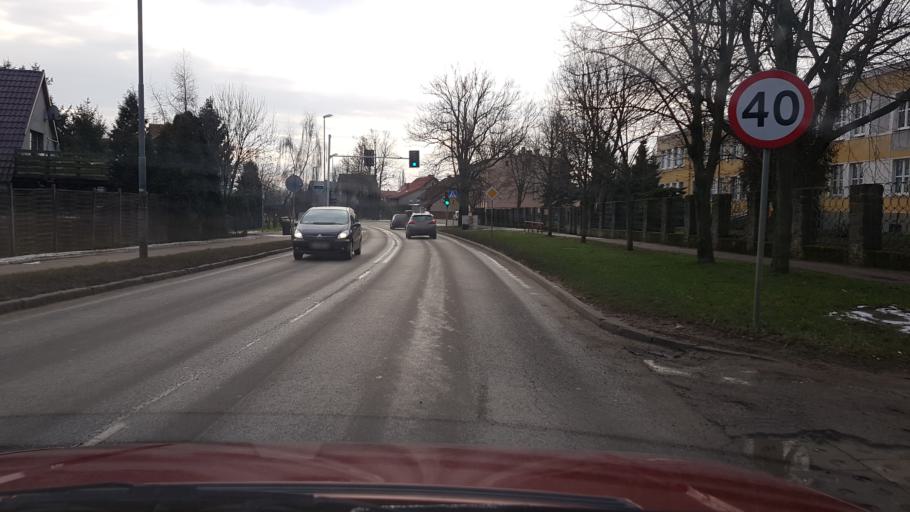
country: PL
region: West Pomeranian Voivodeship
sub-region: Szczecin
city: Szczecin
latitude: 53.4773
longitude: 14.5884
